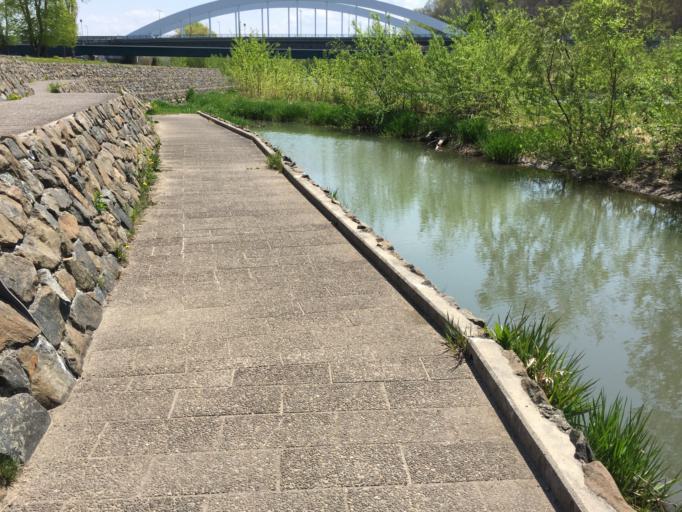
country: JP
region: Hokkaido
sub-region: Asahikawa-shi
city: Asahikawa
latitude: 43.7566
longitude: 142.3653
